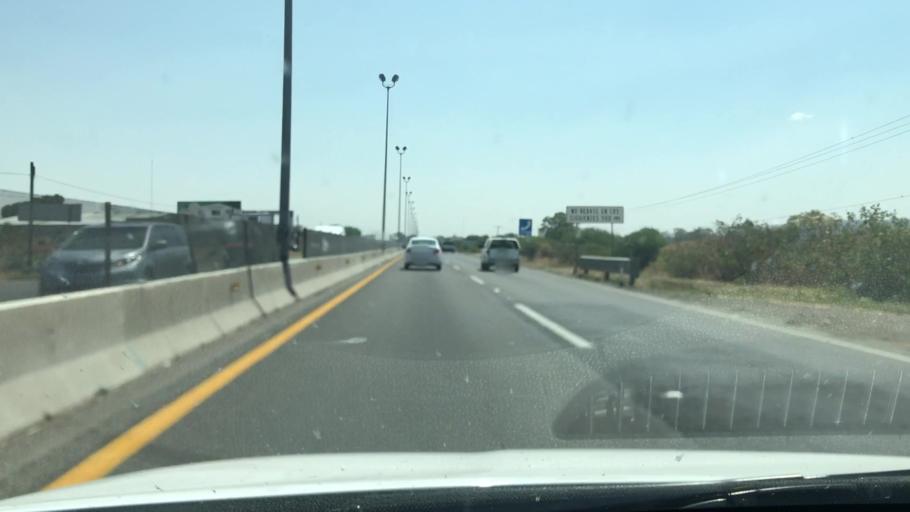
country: MX
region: Guanajuato
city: Abasolo
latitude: 20.4535
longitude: -101.5447
